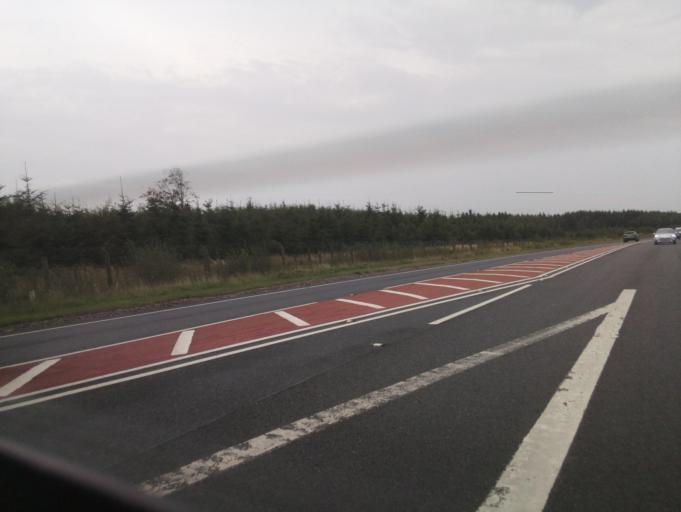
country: GB
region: Scotland
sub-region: Dumfries and Galloway
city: Lockerbie
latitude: 55.0188
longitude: -3.3645
